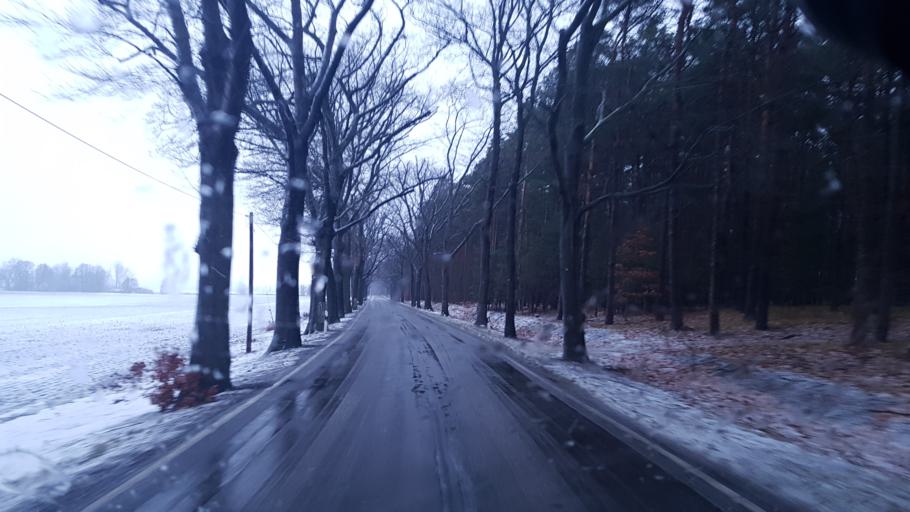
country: DE
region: Brandenburg
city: Tauer
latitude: 51.8954
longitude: 14.4848
